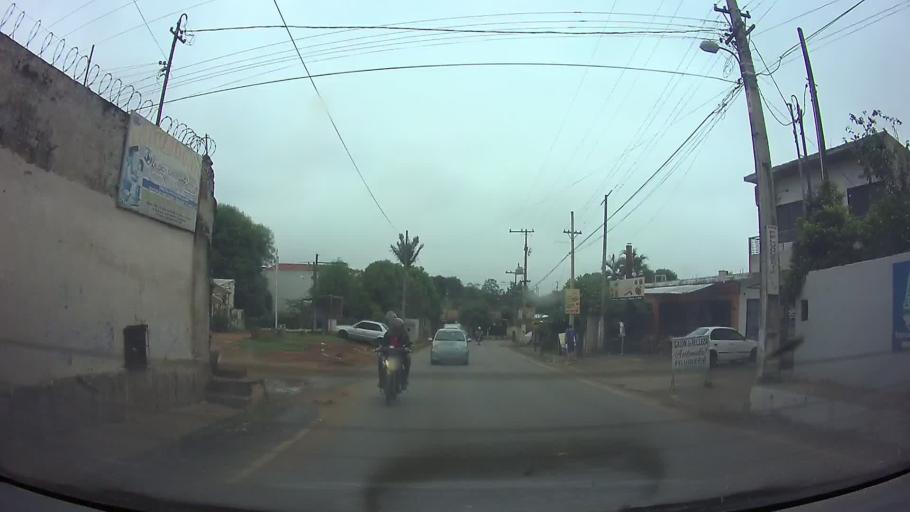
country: PY
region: Central
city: San Lorenzo
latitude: -25.3279
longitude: -57.5044
